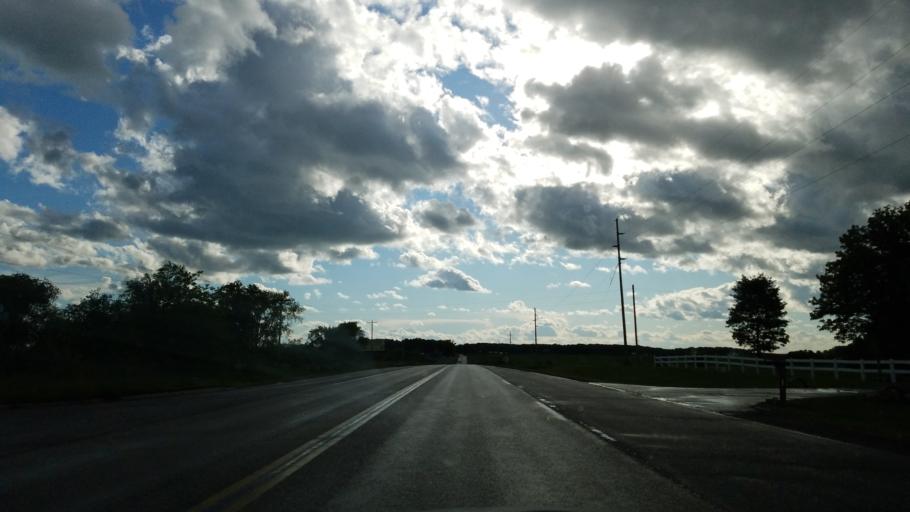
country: US
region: Wisconsin
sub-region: Polk County
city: Osceola
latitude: 45.3432
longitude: -92.6515
